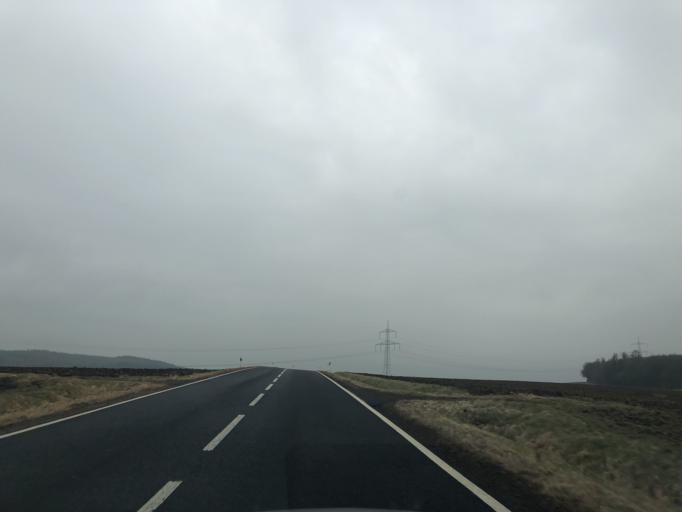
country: DE
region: Hesse
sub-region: Regierungsbezirk Darmstadt
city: Birstein
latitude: 50.3681
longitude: 9.3056
